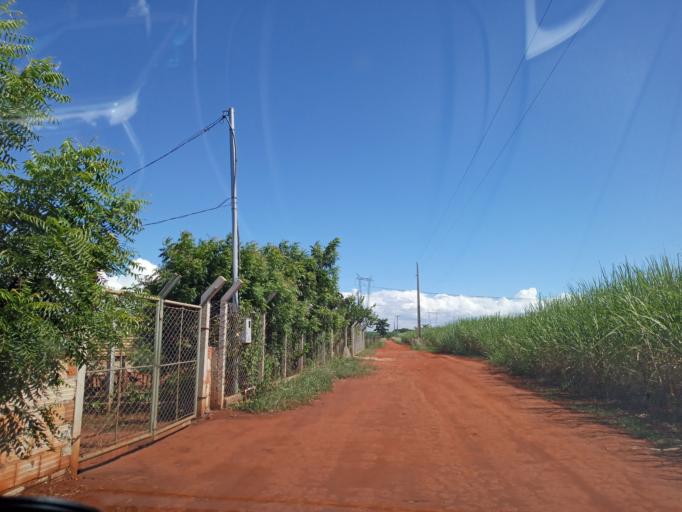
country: BR
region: Goias
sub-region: Itumbiara
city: Itumbiara
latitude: -18.4335
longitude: -49.1176
